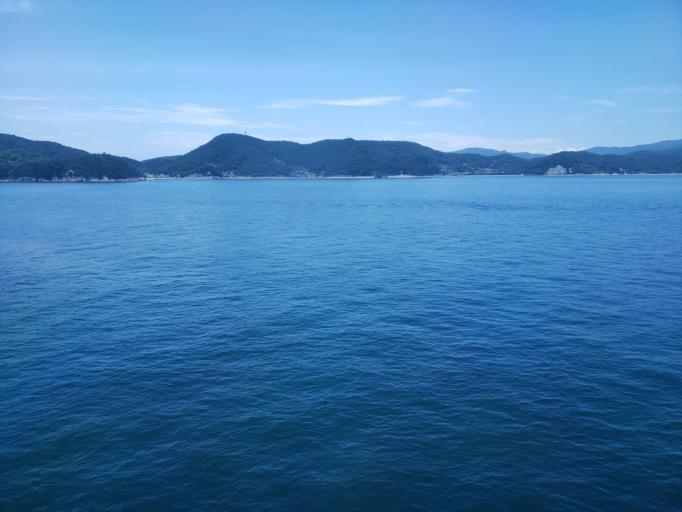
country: JP
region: Kagawa
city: Tonosho
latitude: 34.4183
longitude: 134.2631
